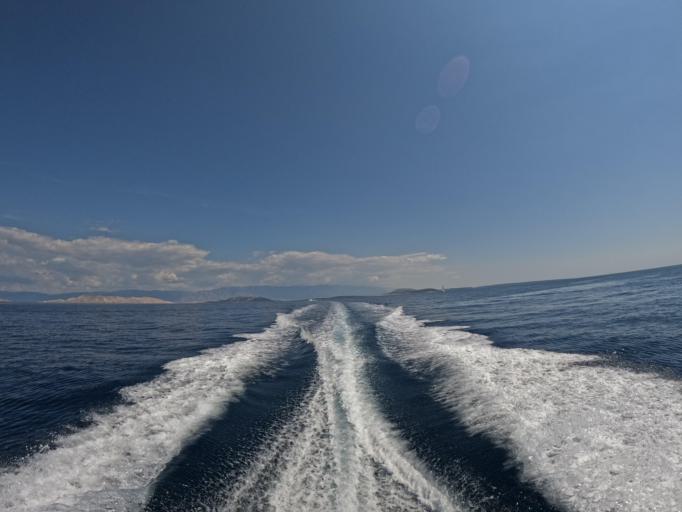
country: HR
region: Primorsko-Goranska
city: Punat
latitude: 44.8956
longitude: 14.6213
